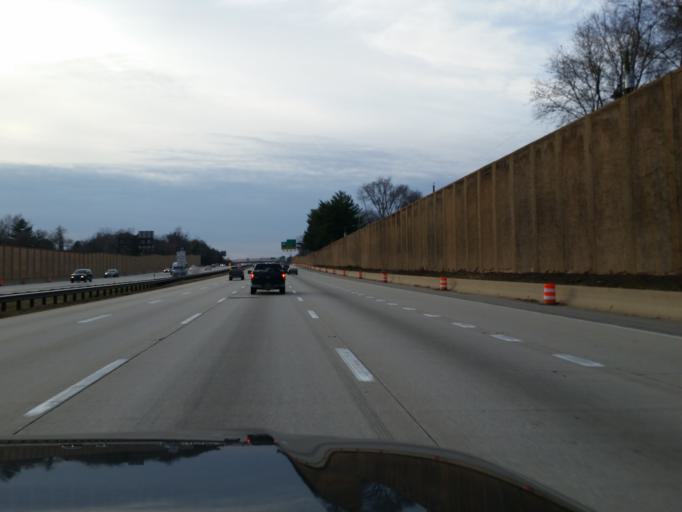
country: US
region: Maryland
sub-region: Prince George's County
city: Bowie
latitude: 38.9535
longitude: -76.7297
